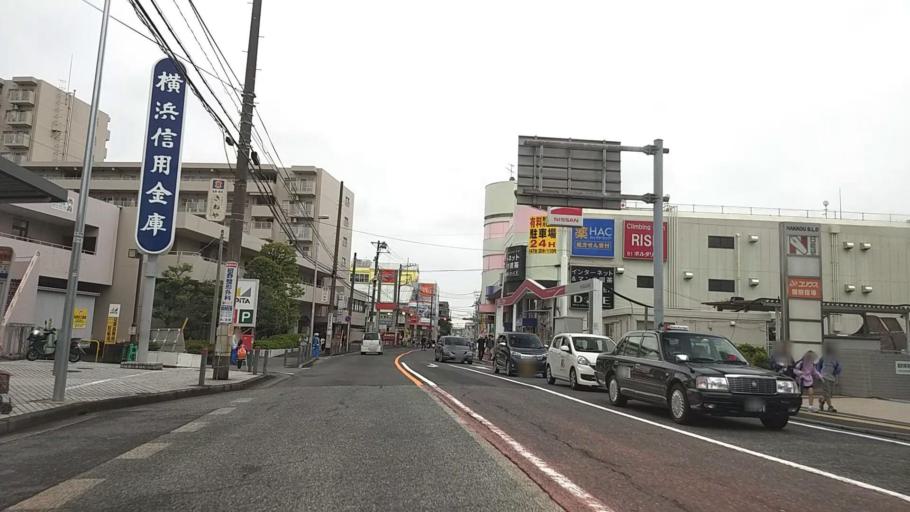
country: JP
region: Kanagawa
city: Fujisawa
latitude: 35.3992
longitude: 139.5364
